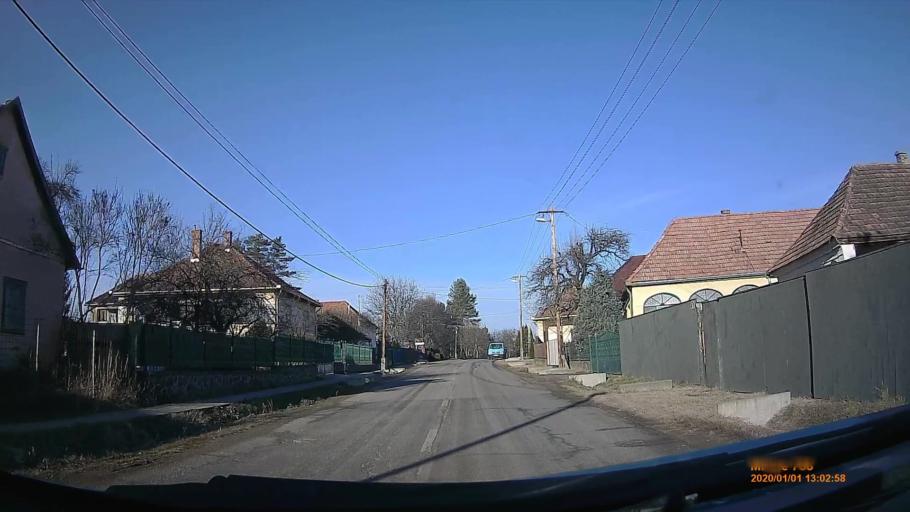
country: HU
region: Heves
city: Parad
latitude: 47.9389
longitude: 20.0239
